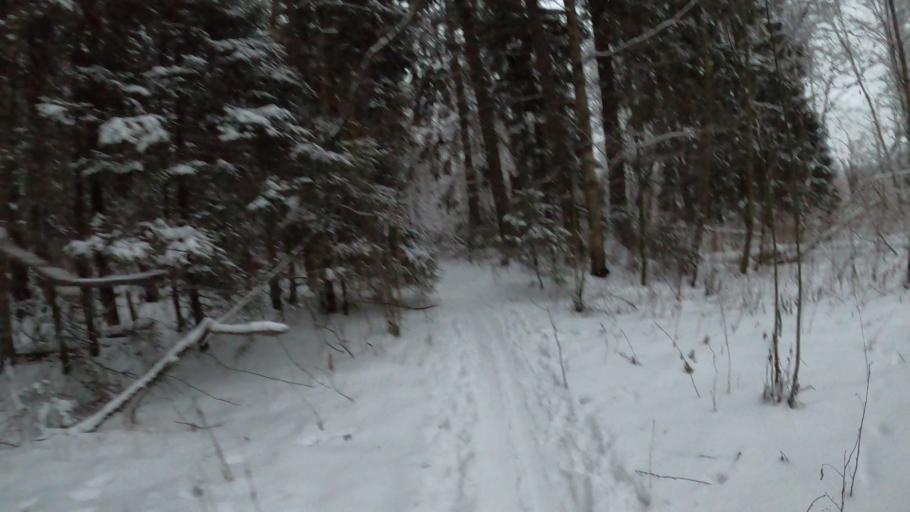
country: RU
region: Moskovskaya
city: Nakhabino
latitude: 55.8974
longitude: 37.2051
